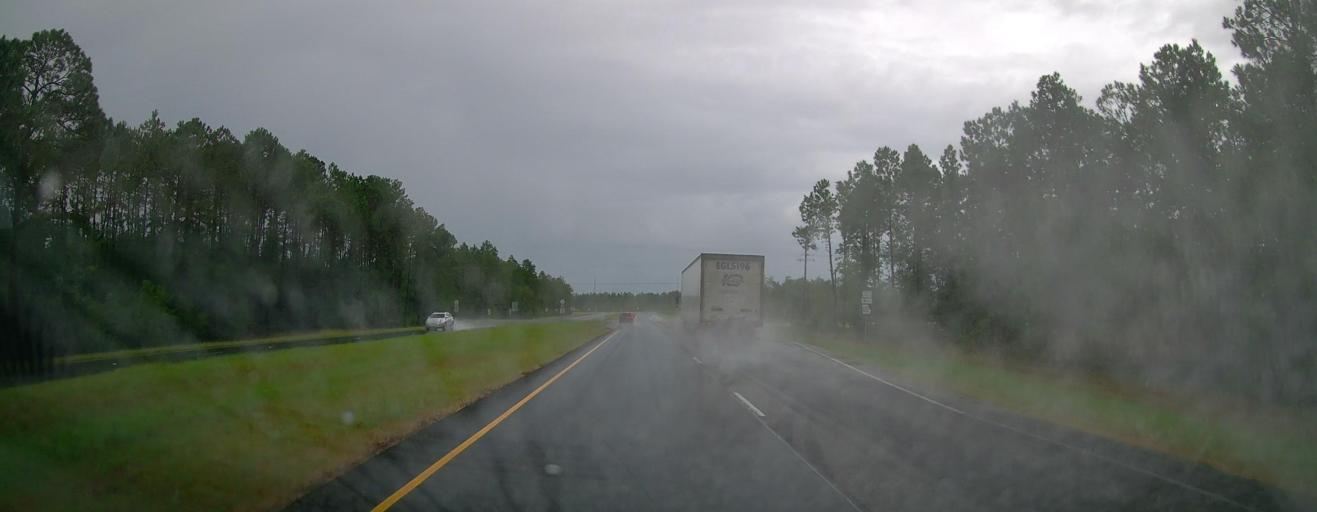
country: US
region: Georgia
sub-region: Ware County
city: Deenwood
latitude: 31.2139
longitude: -82.4189
